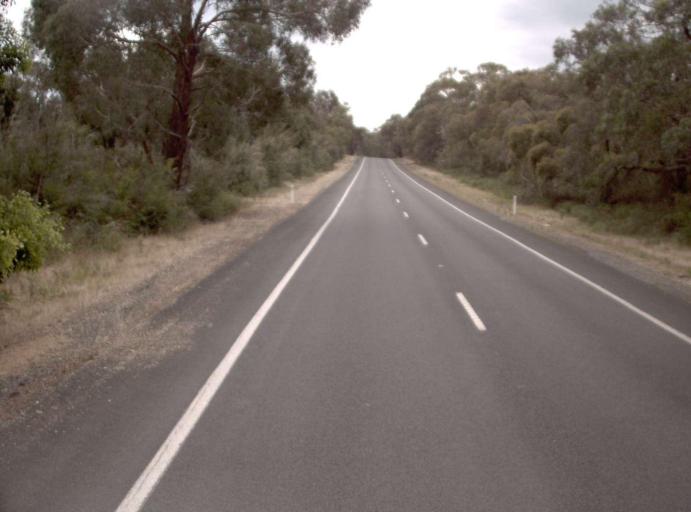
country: AU
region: Victoria
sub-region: Wellington
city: Sale
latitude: -38.2636
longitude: 147.0361
